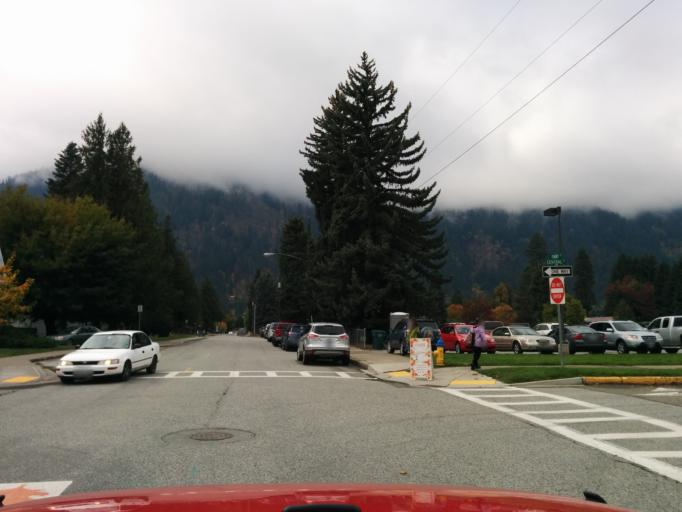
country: US
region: Washington
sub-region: Chelan County
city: Leavenworth
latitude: 47.5970
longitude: -120.6633
